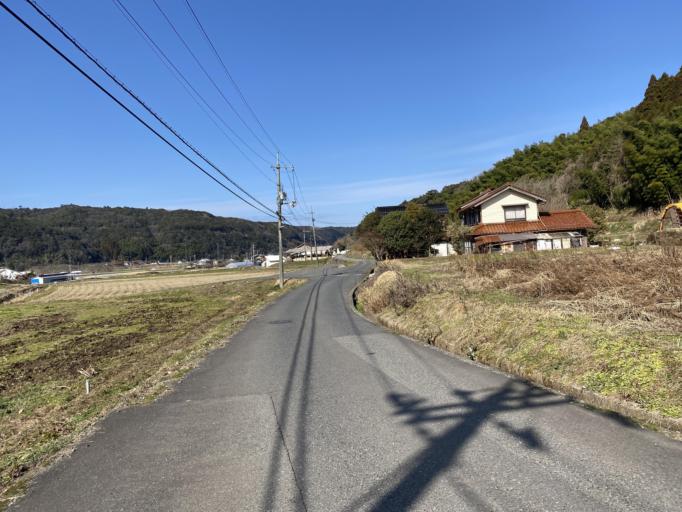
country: JP
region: Tottori
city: Kurayoshi
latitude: 35.4928
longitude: 133.9882
